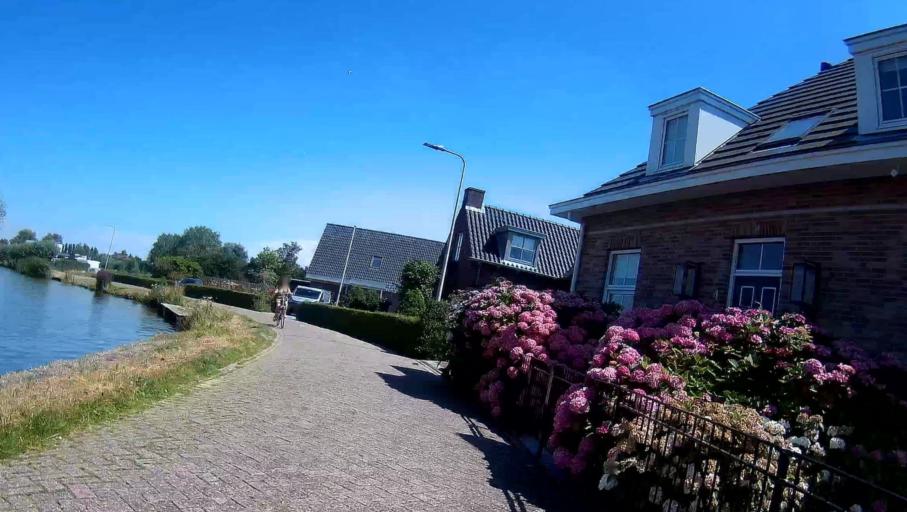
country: NL
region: South Holland
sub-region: Gemeente Westland
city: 's-Gravenzande
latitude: 52.0073
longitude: 4.1764
